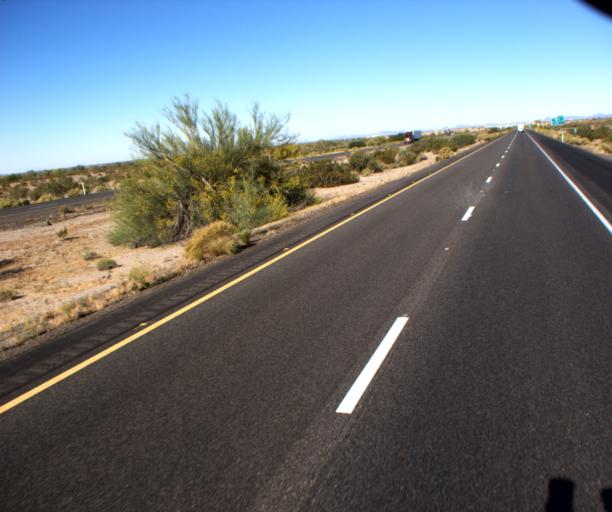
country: US
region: Arizona
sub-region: Maricopa County
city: Gila Bend
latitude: 32.9231
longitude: -112.6605
